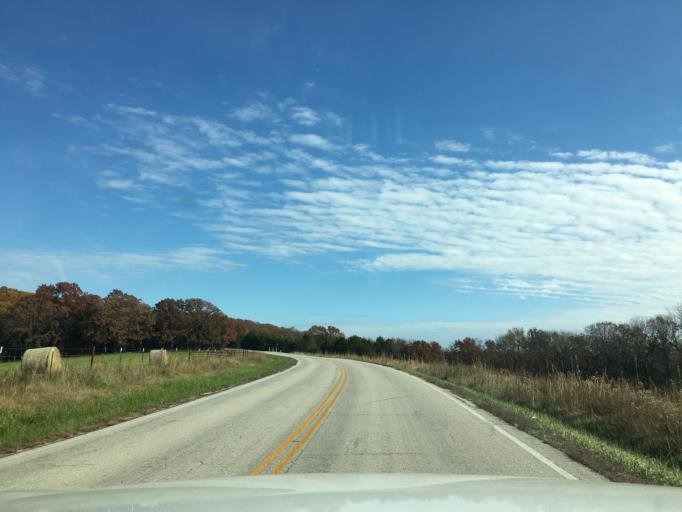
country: US
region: Missouri
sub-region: Maries County
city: Belle
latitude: 38.3354
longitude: -91.7784
